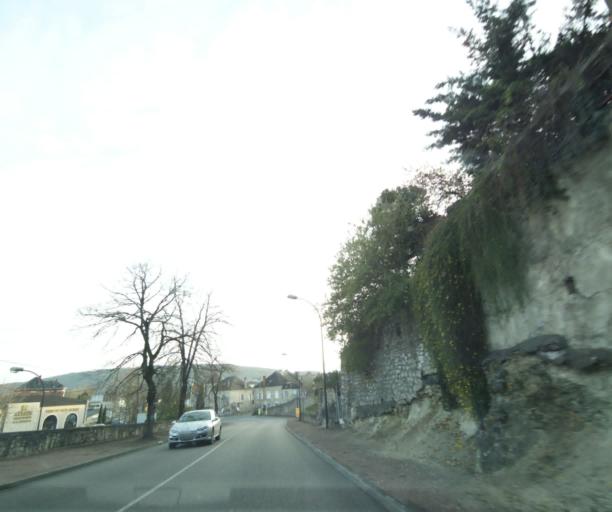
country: FR
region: Midi-Pyrenees
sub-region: Departement du Lot
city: Souillac
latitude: 44.9019
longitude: 1.4776
